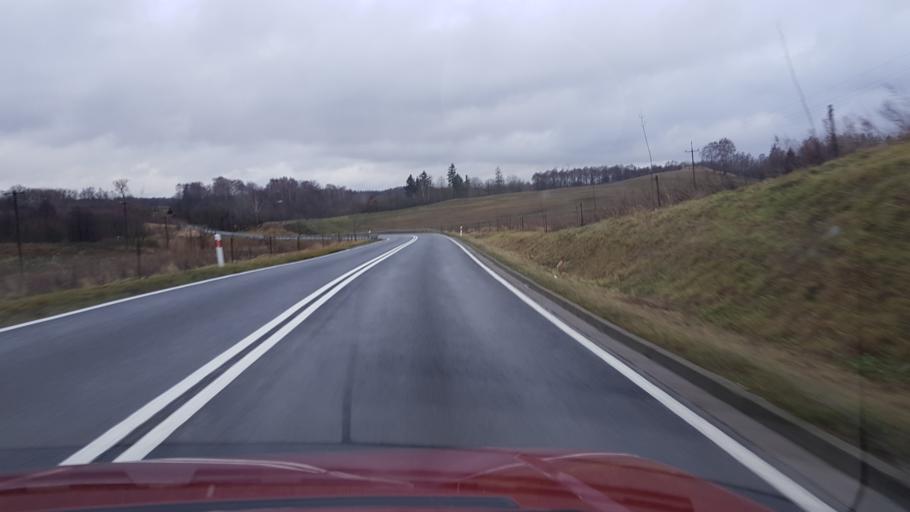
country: PL
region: West Pomeranian Voivodeship
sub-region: Powiat lobeski
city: Wegorzyno
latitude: 53.5288
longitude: 15.5783
